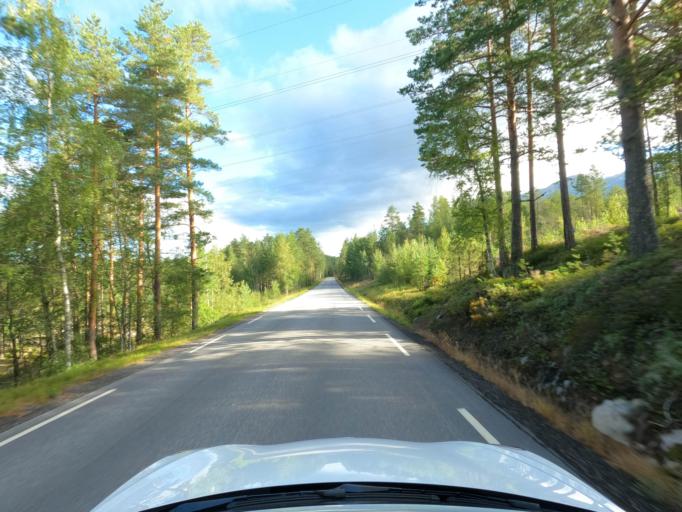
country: NO
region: Telemark
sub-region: Hjartdal
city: Sauland
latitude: 59.7687
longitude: 9.0920
